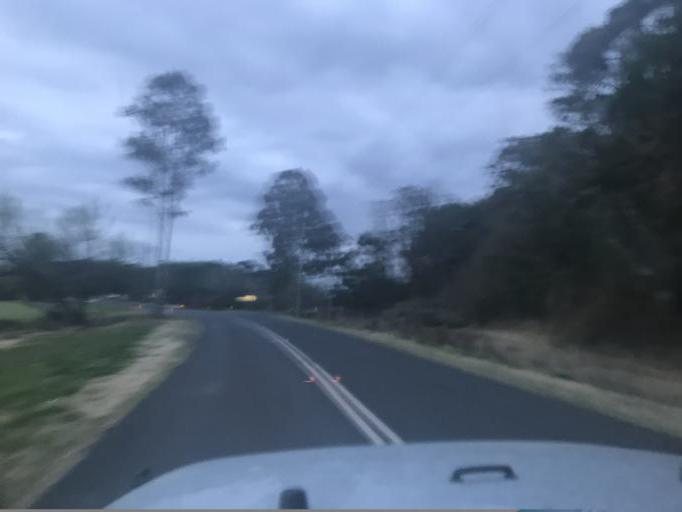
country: AU
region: New South Wales
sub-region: Hawkesbury
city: Pitt Town
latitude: -33.5044
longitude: 150.8754
